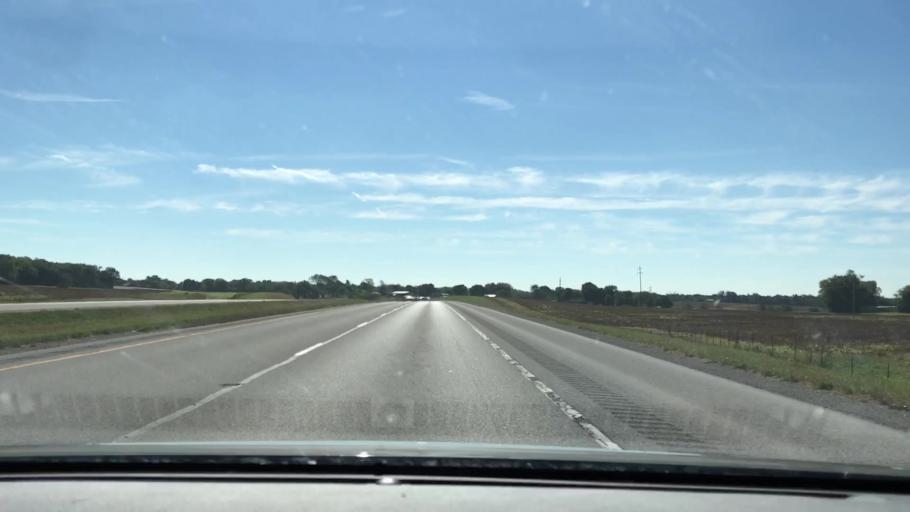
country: US
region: Kentucky
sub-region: Todd County
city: Elkton
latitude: 36.8149
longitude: -87.1406
